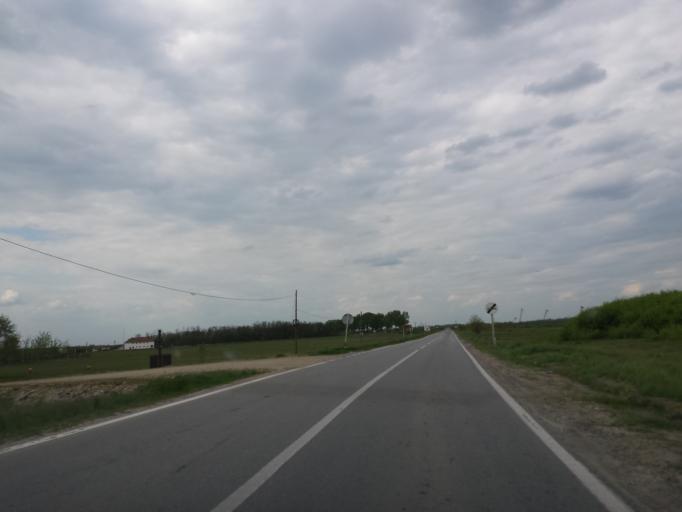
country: RO
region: Timis
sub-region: Comuna Cenad
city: Cenad
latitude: 46.1128
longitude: 20.5949
